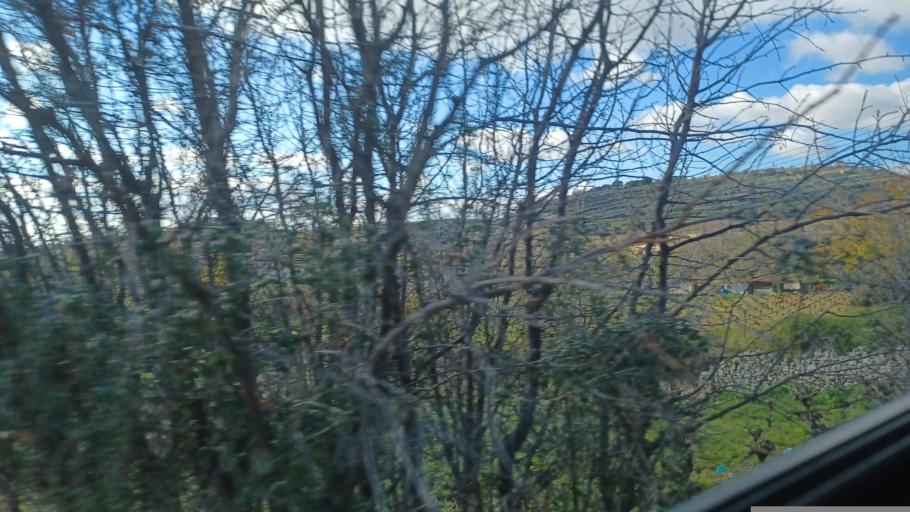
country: CY
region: Limassol
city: Pachna
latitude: 34.8297
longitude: 32.7891
